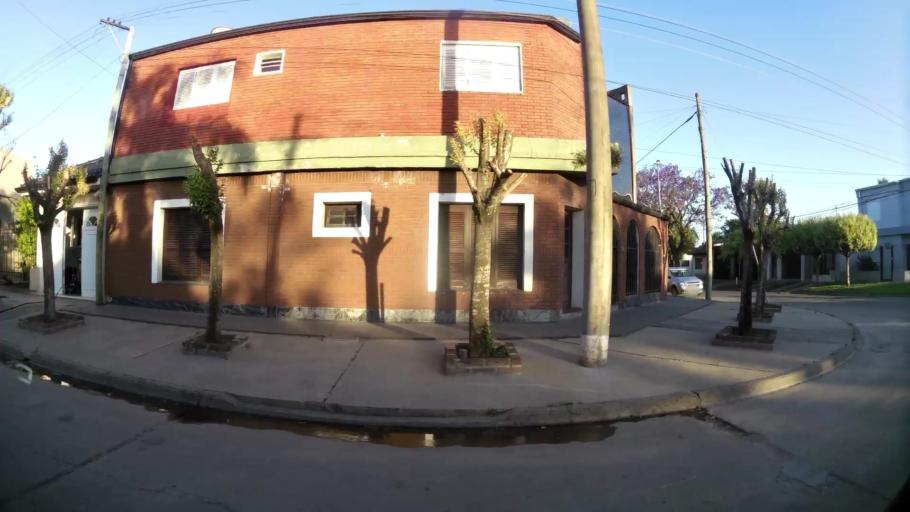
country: AR
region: Santa Fe
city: Santa Fe de la Vera Cruz
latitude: -31.5989
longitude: -60.6887
